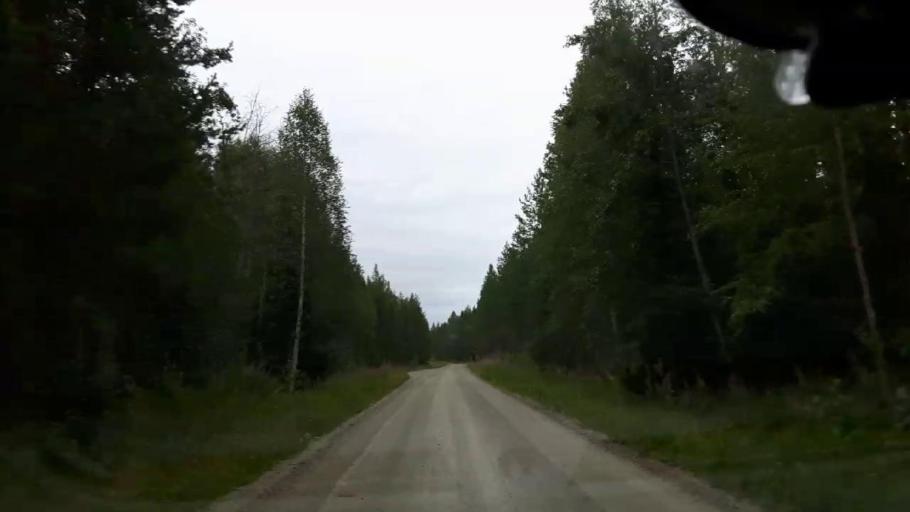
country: SE
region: Jaemtland
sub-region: Braecke Kommun
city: Braecke
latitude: 62.8231
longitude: 15.7136
